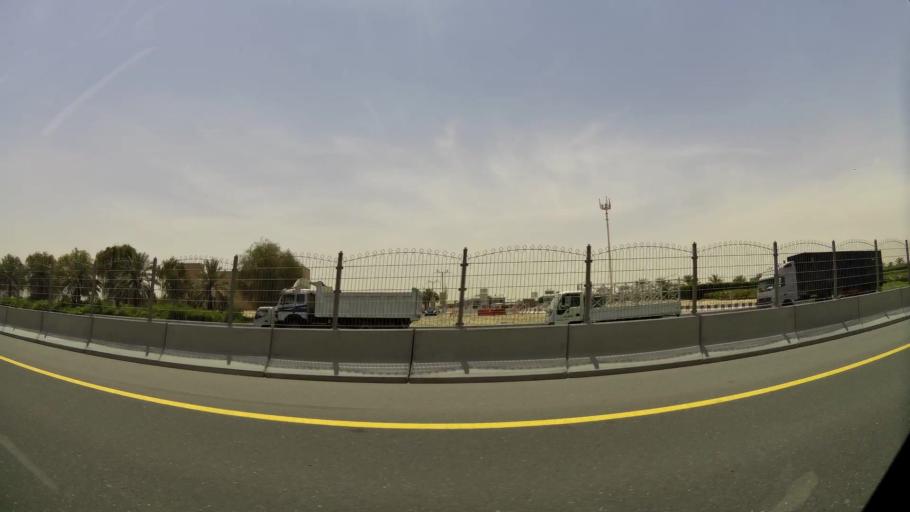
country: AE
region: Dubai
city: Dubai
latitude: 25.1039
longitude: 55.3376
